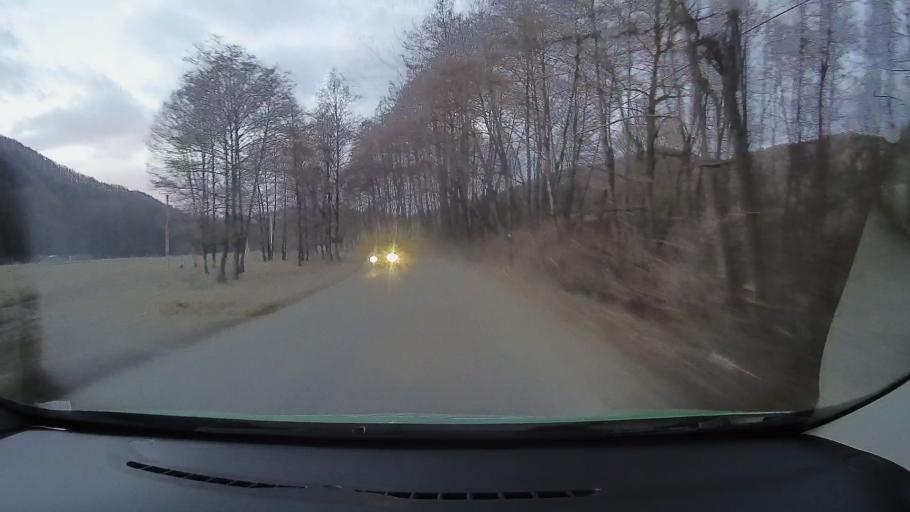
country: RO
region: Dambovita
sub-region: Comuna Valea Lunga
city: Valea Lunga-Cricov
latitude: 45.0851
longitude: 25.5805
